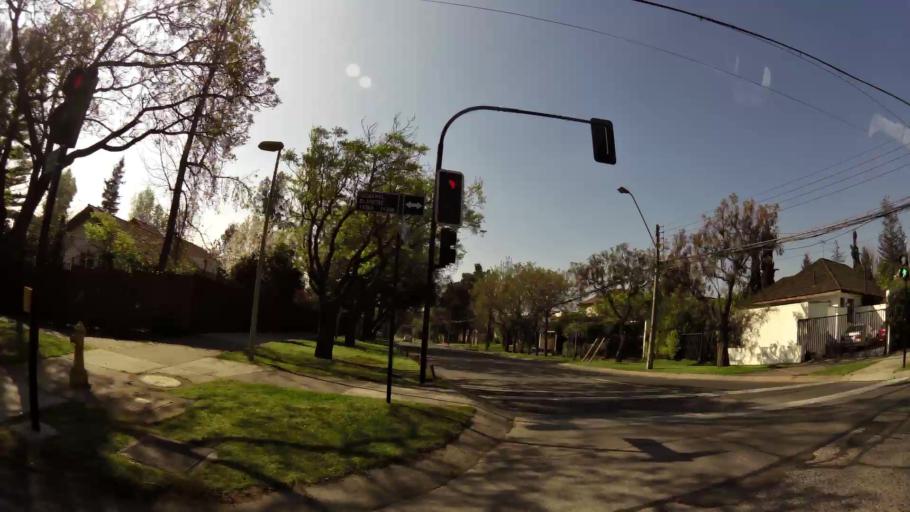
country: CL
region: Santiago Metropolitan
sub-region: Provincia de Santiago
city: Villa Presidente Frei, Nunoa, Santiago, Chile
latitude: -33.4034
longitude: -70.5195
